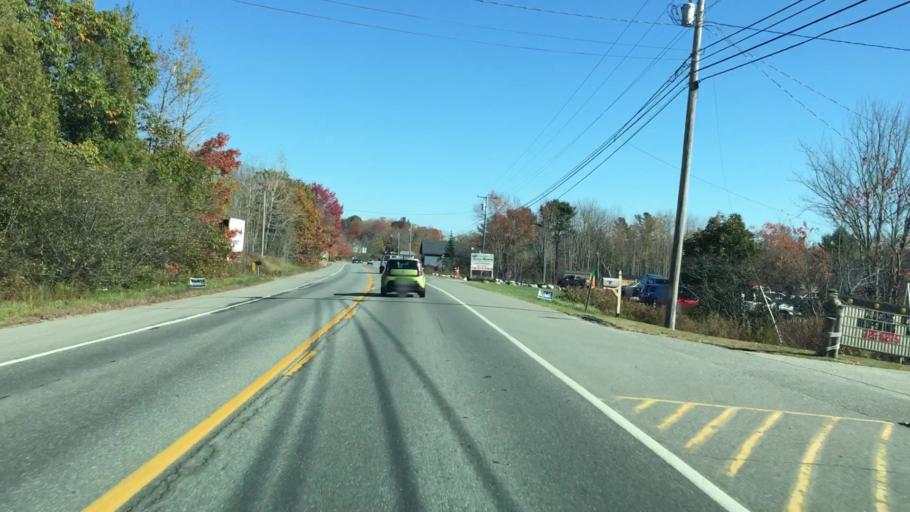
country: US
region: Maine
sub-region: Waldo County
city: Stockton Springs
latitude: 44.4782
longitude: -68.8768
